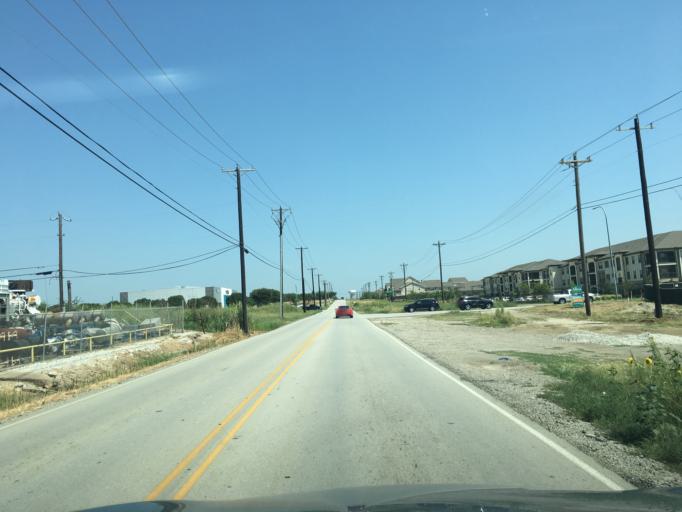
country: US
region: Texas
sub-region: Tarrant County
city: Blue Mound
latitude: 32.9047
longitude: -97.3317
